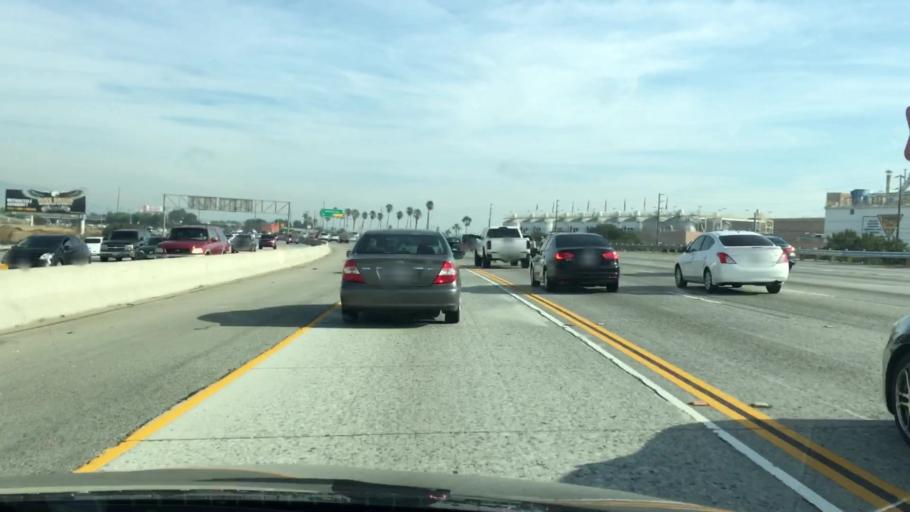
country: US
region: California
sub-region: Los Angeles County
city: Irwindale
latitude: 34.1288
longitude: -117.9415
